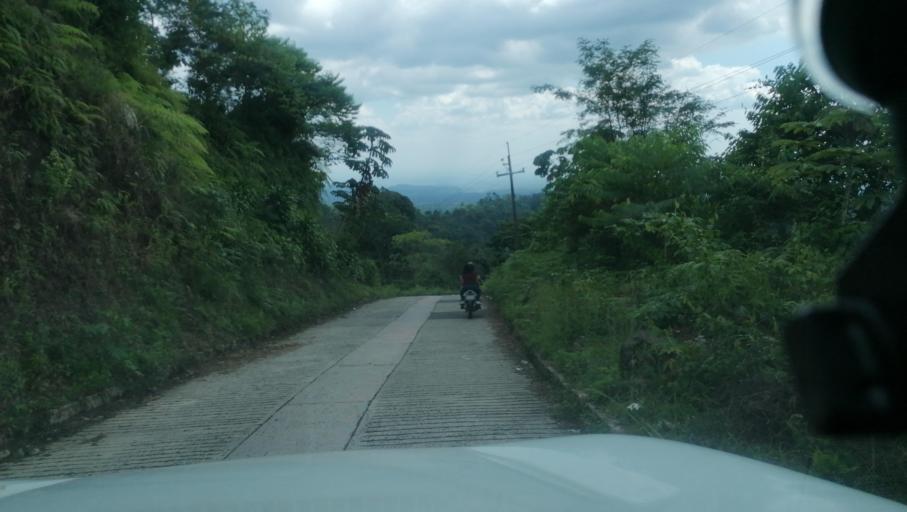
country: MX
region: Chiapas
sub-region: Cacahoatan
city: Benito Juarez
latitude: 15.0669
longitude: -92.1516
